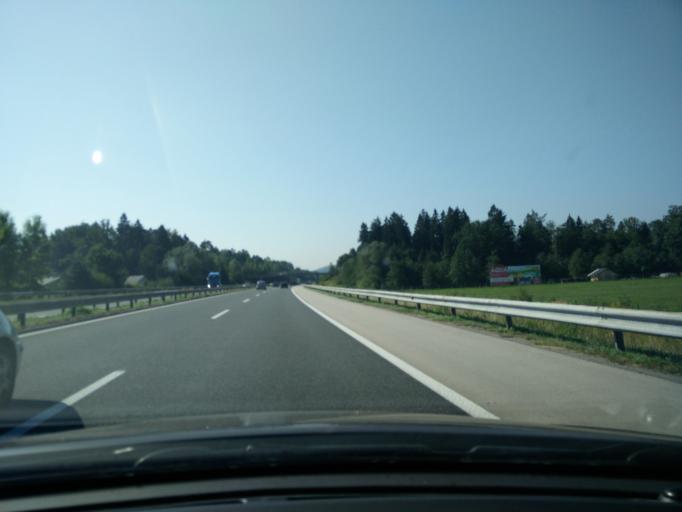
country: SI
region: Vodice
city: Vodice
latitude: 46.1693
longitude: 14.4856
